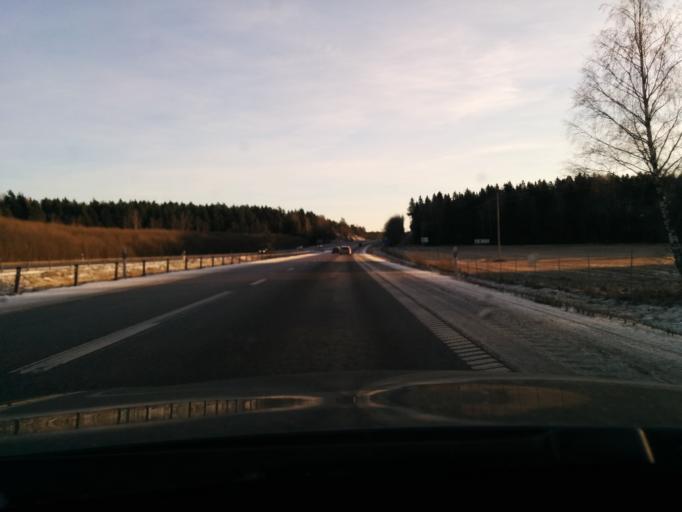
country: SE
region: Stockholm
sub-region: Upplands-Bro Kommun
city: Bro
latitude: 59.5405
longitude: 17.6131
